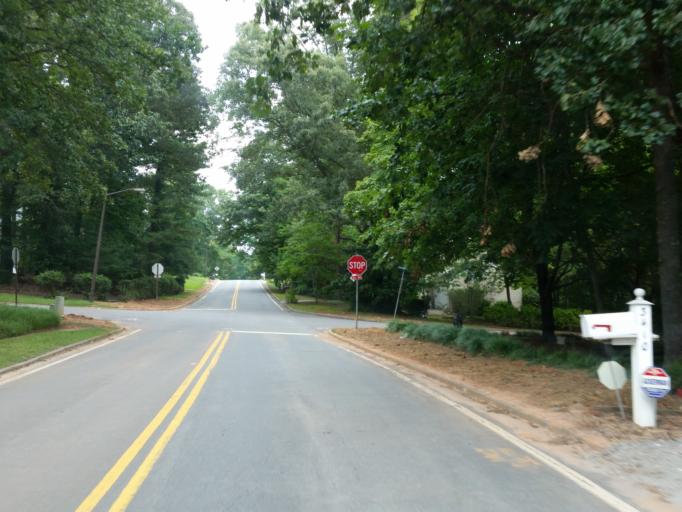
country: US
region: Georgia
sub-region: Fulton County
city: Sandy Springs
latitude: 33.9540
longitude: -84.4541
